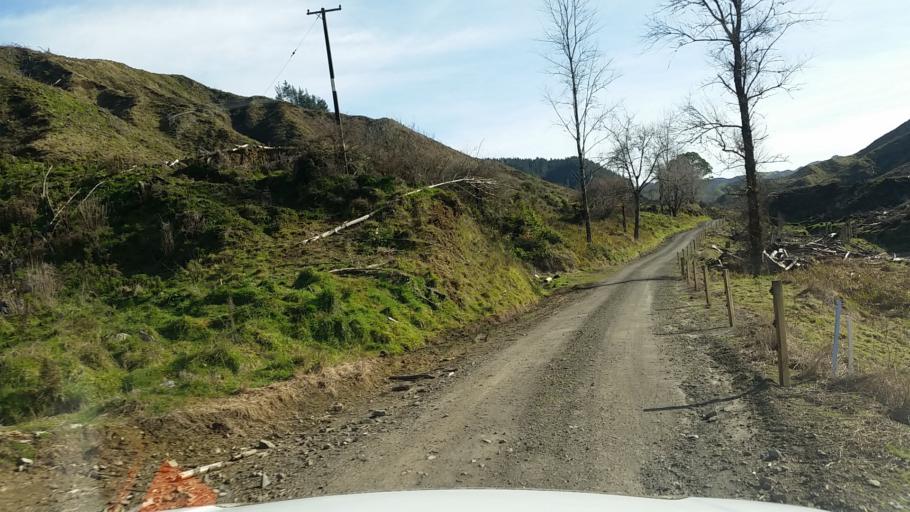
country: NZ
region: Taranaki
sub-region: South Taranaki District
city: Eltham
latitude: -39.3655
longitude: 174.5176
